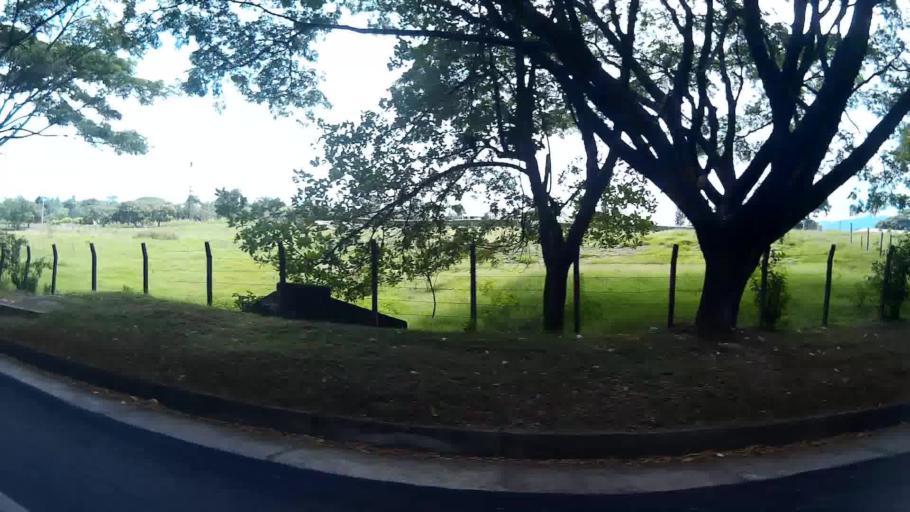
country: CO
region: Risaralda
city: Pereira
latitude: 4.8135
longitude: -75.7962
